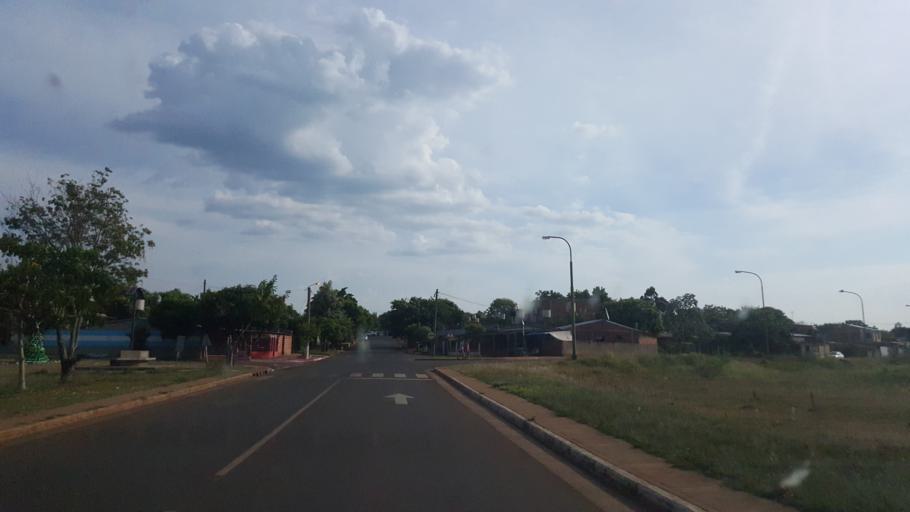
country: AR
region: Misiones
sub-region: Departamento de Capital
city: Posadas
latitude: -27.4186
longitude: -55.8860
